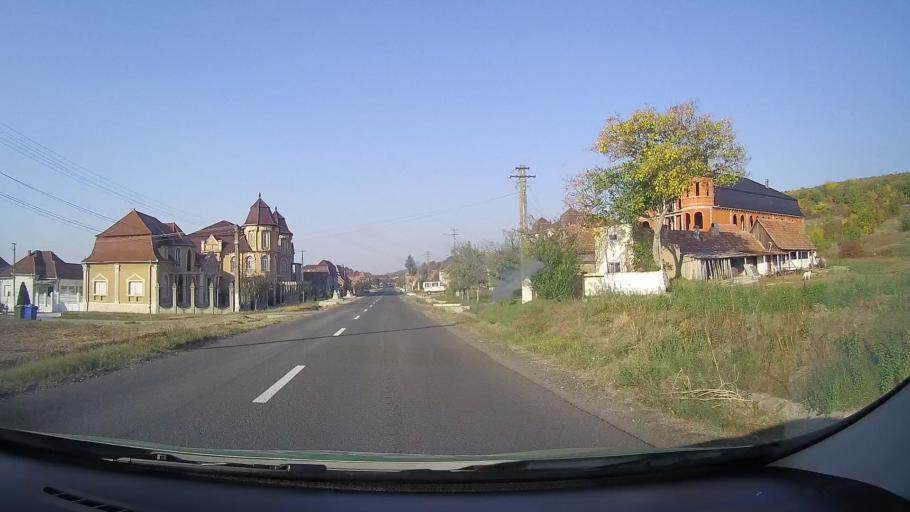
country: RO
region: Arad
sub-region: Comuna Covasint
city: Covasint
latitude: 46.1926
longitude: 21.6058
